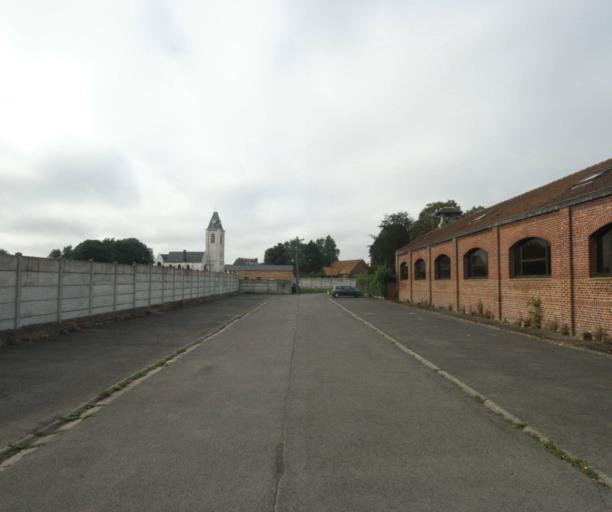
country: FR
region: Nord-Pas-de-Calais
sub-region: Departement du Nord
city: Villeneuve-d'Ascq
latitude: 50.6286
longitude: 3.1498
